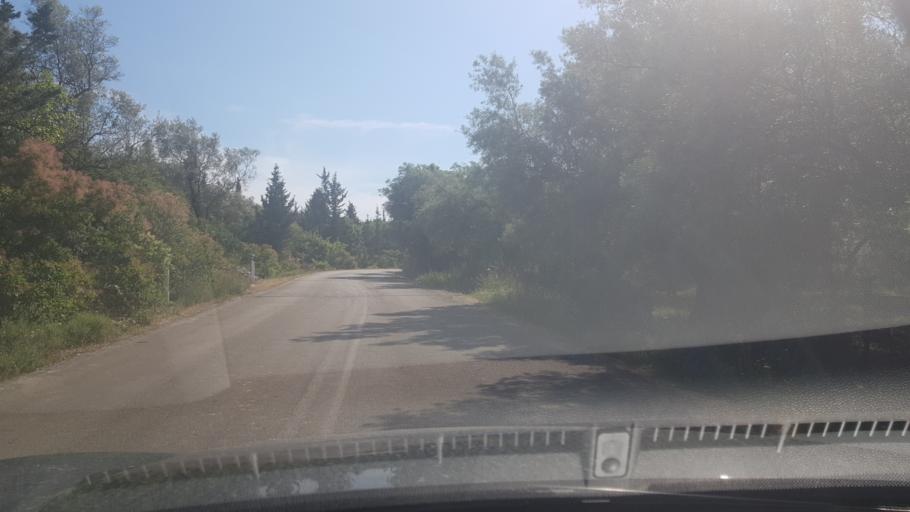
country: GR
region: Ionian Islands
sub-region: Lefkada
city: Nidri
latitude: 38.6515
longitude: 20.6689
